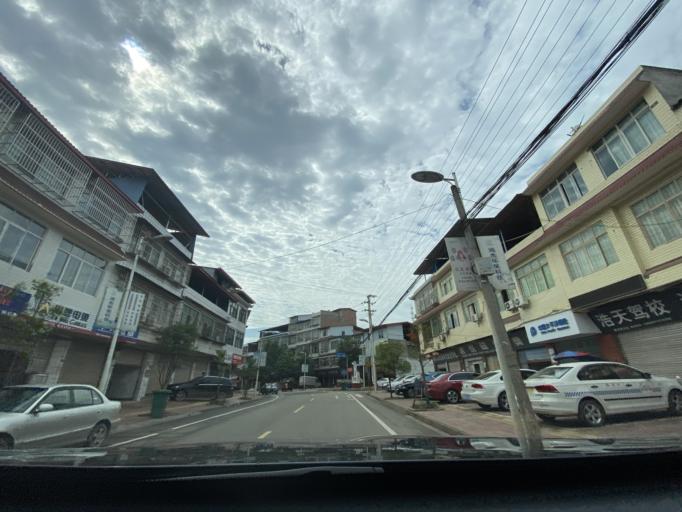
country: CN
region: Sichuan
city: Jiancheng
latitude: 30.4871
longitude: 104.6315
